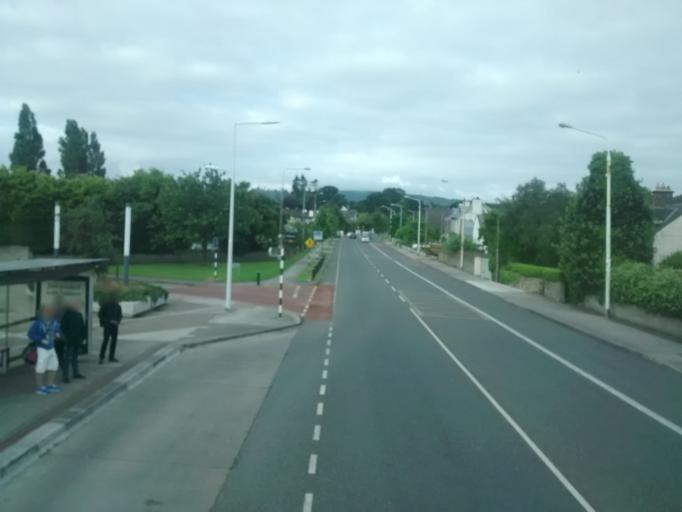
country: IE
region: Leinster
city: Cabinteely
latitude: 53.2779
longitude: -6.1647
